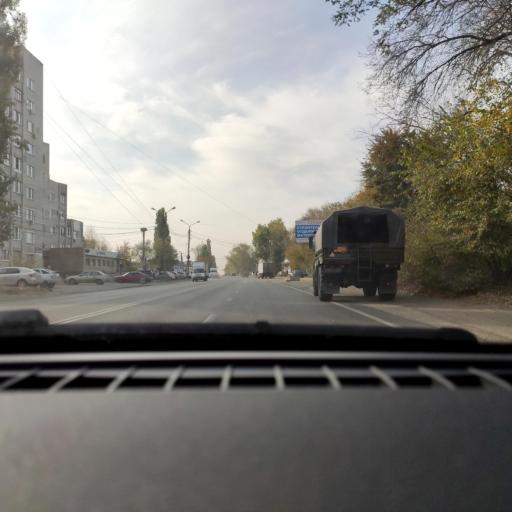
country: RU
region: Voronezj
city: Maslovka
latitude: 51.6002
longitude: 39.2527
